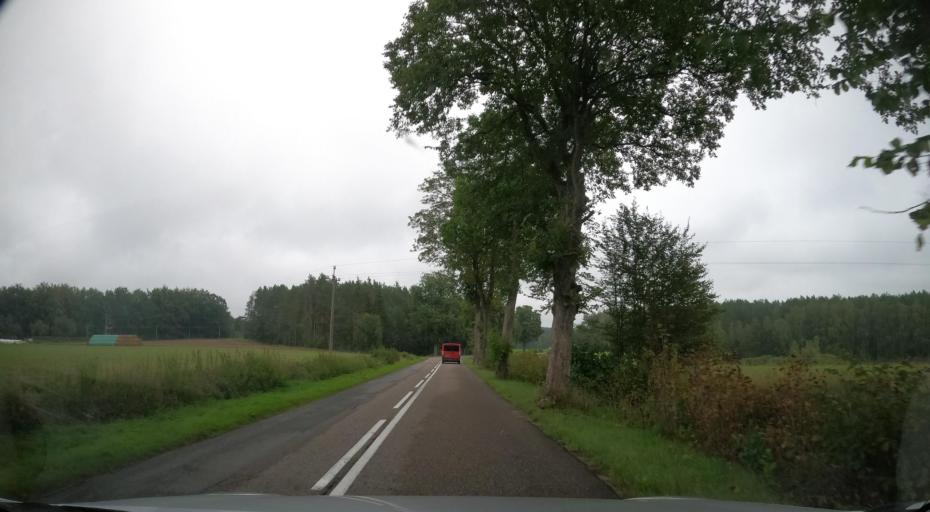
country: PL
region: Pomeranian Voivodeship
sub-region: Powiat wejherowski
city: Luzino
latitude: 54.4883
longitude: 18.1155
